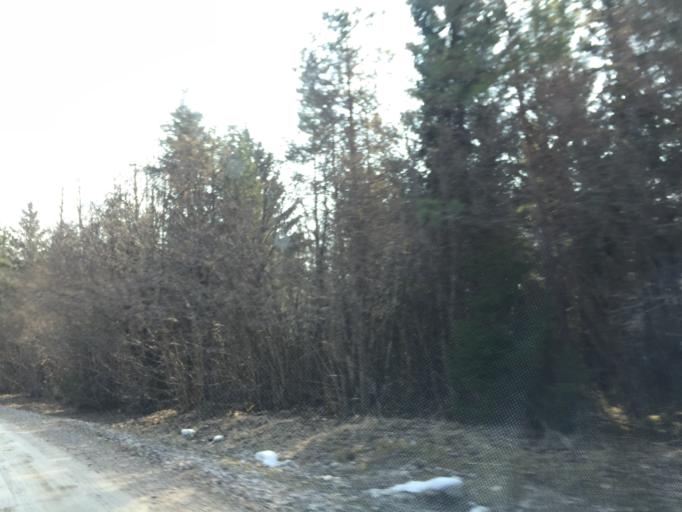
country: EE
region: Saare
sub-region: Kuressaare linn
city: Kuressaare
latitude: 58.3780
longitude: 22.7255
